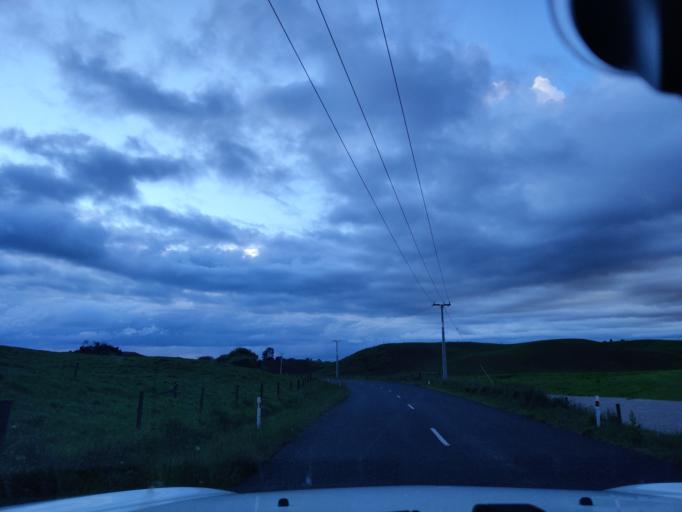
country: NZ
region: Waikato
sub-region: South Waikato District
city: Tokoroa
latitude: -38.1745
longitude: 175.7742
